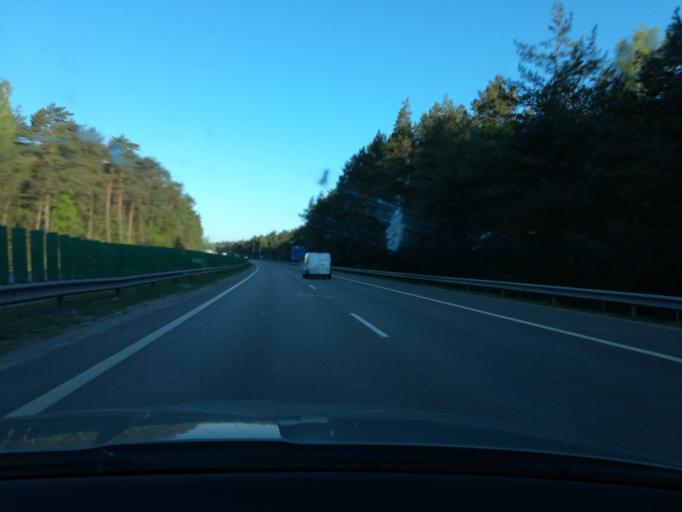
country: LT
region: Vilnius County
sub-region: Vilniaus Rajonas
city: Vievis
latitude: 54.7661
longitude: 24.8481
